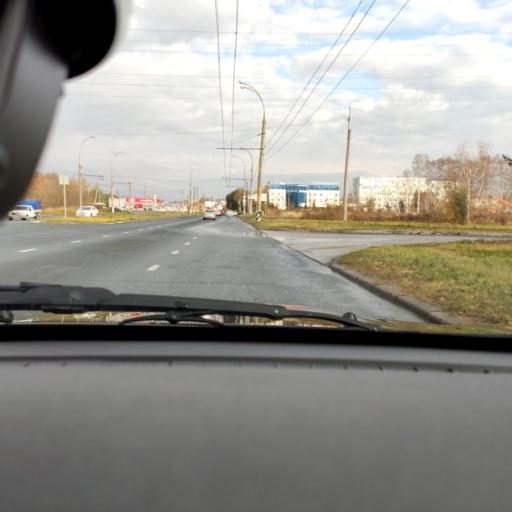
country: RU
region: Samara
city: Tol'yatti
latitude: 53.5500
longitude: 49.3027
